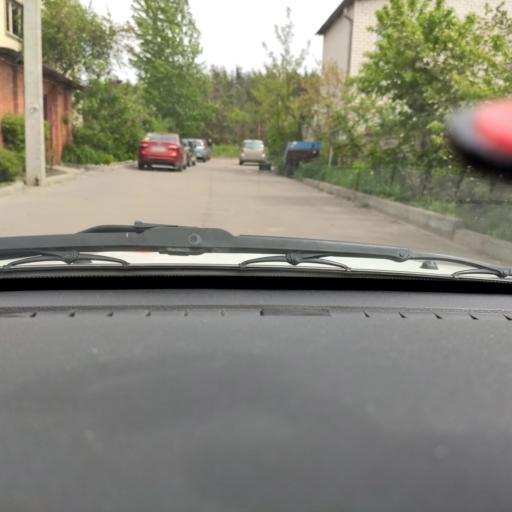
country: RU
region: Voronezj
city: Podgornoye
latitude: 51.7372
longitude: 39.1685
